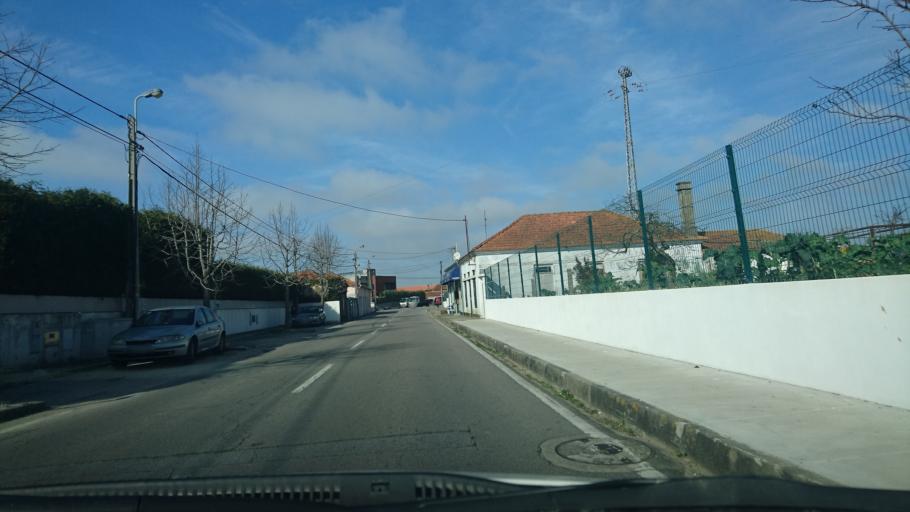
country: PT
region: Aveiro
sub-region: Espinho
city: Souto
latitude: 40.9856
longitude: -8.6320
